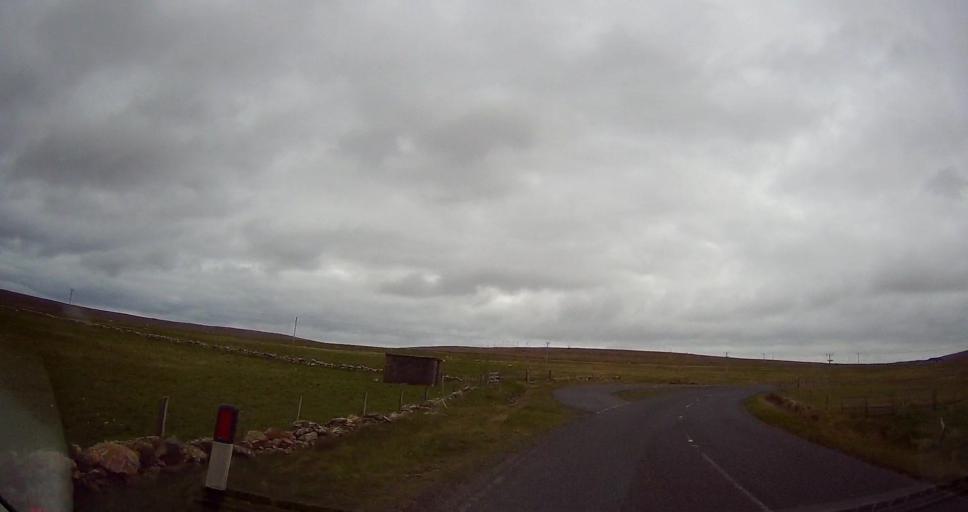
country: GB
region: Scotland
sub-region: Shetland Islands
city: Shetland
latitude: 60.7564
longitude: -0.8768
